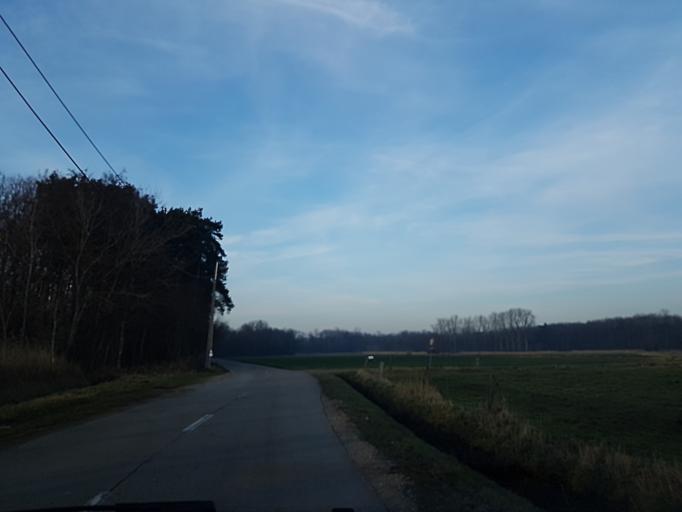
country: BE
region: Flanders
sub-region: Provincie Antwerpen
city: Zandhoven
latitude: 51.2491
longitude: 4.6470
